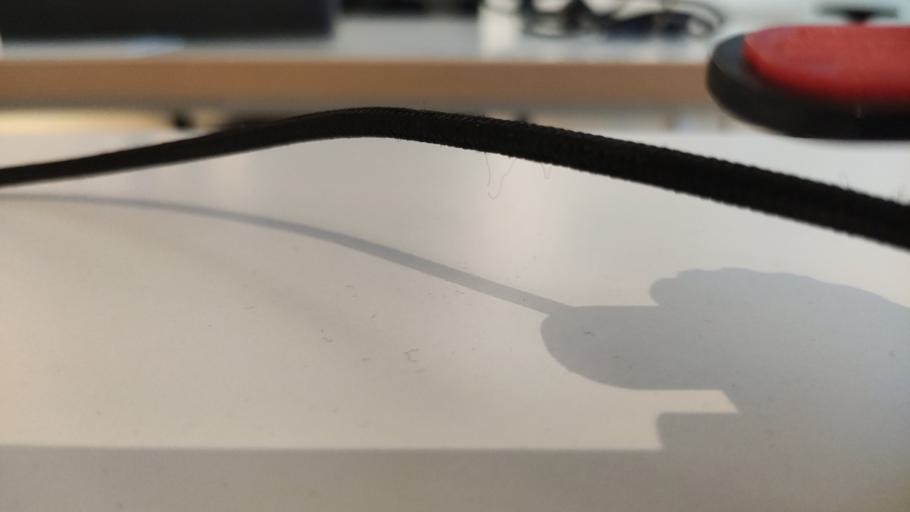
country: RU
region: Moskovskaya
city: Novopetrovskoye
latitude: 55.8678
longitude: 36.3947
